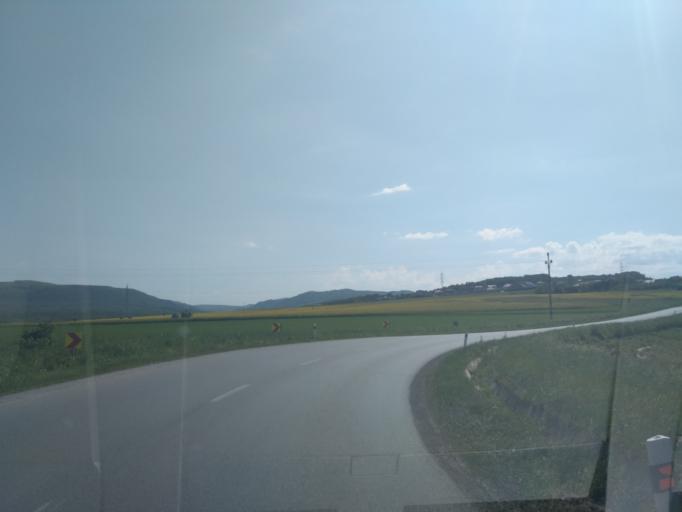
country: SK
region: Presovsky
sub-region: Okres Presov
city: Presov
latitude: 48.9508
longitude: 21.2826
